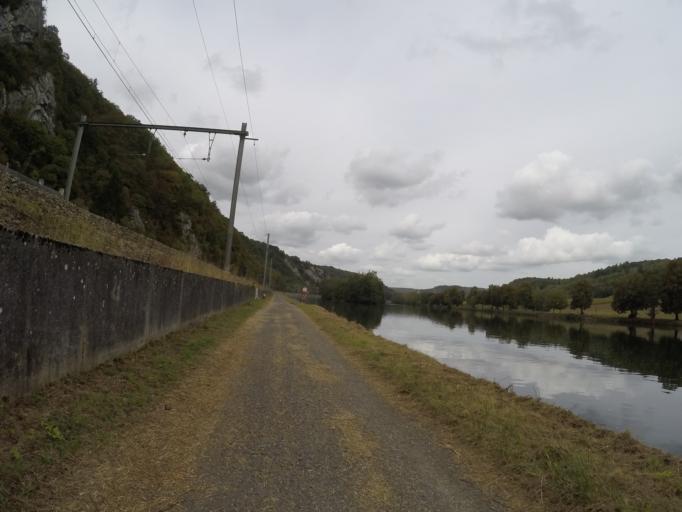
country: BE
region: Wallonia
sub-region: Province de Namur
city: Dinant
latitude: 50.2794
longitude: 4.8933
